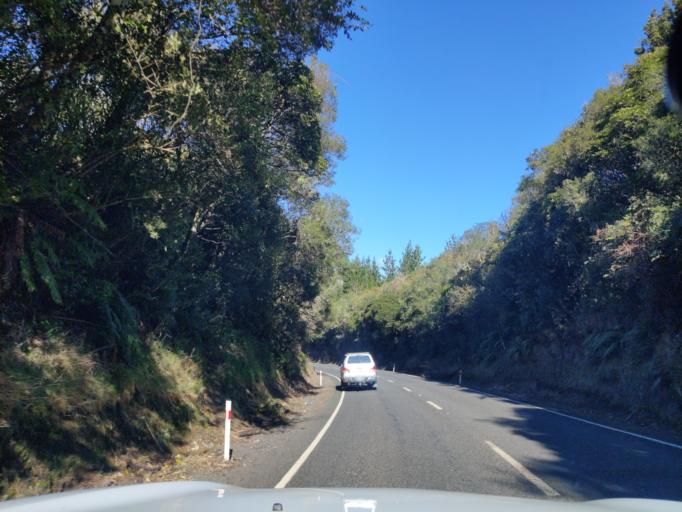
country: NZ
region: Waikato
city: Turangi
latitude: -38.7530
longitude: 175.6754
